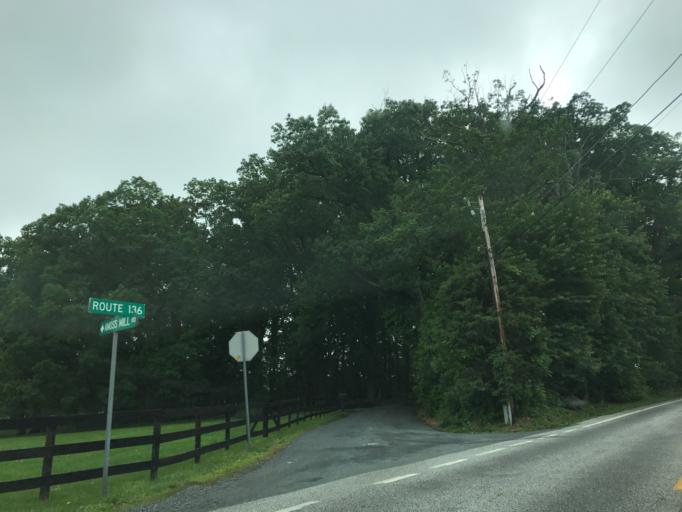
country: US
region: Maryland
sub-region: Harford County
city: Jarrettsville
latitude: 39.7019
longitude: -76.4895
